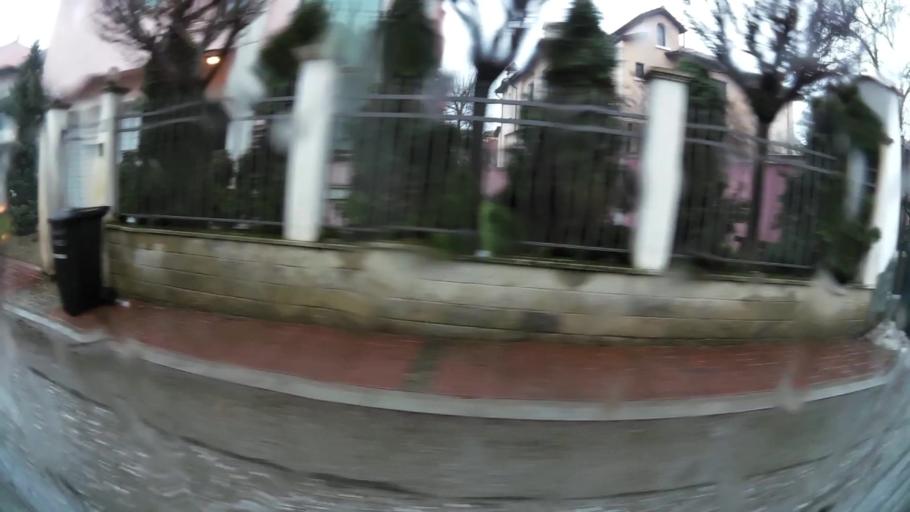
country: BG
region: Sofia-Capital
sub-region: Stolichna Obshtina
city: Sofia
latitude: 42.6266
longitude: 23.3641
